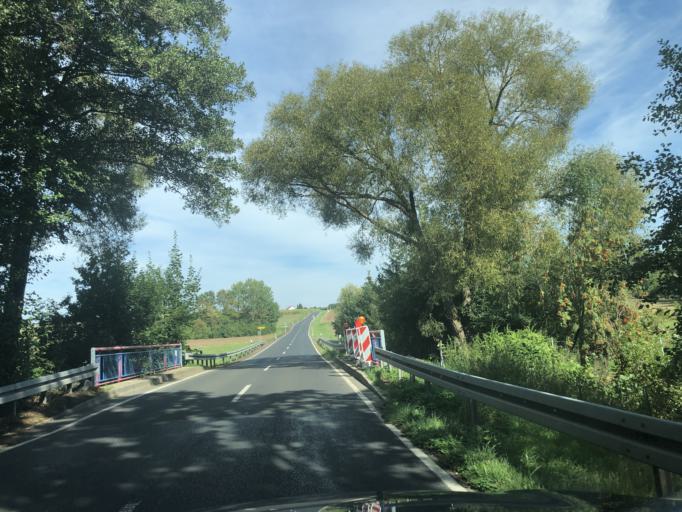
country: DE
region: Bavaria
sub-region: Upper Palatinate
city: Pressath
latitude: 49.7865
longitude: 11.9234
